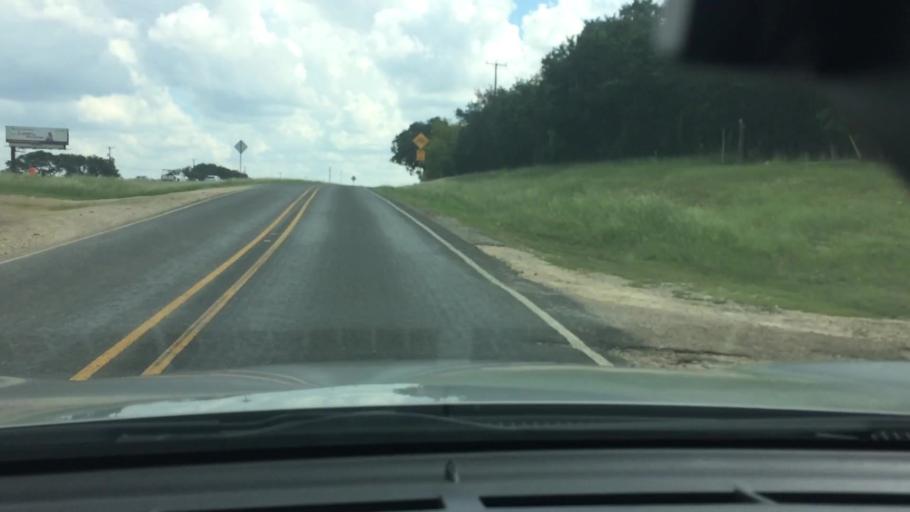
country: US
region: Texas
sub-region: Bexar County
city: Scenic Oaks
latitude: 29.7376
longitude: -98.6869
